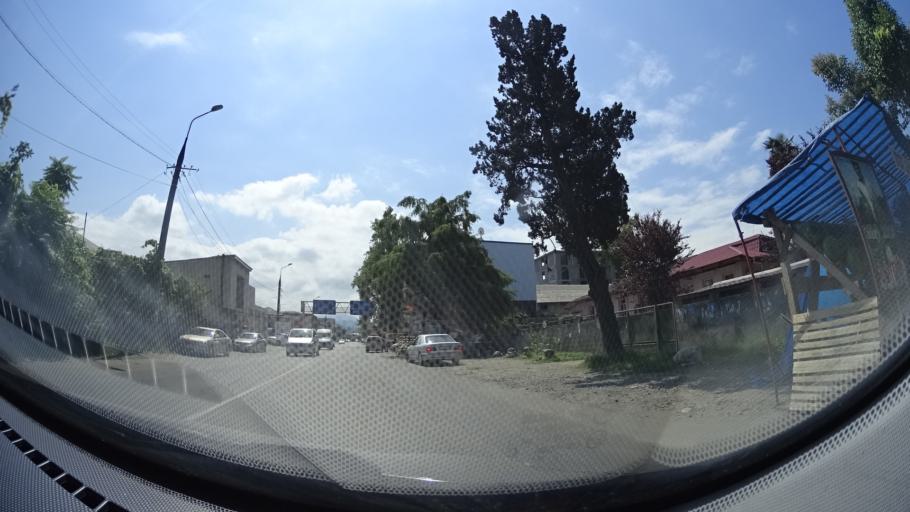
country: GE
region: Ajaria
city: Batumi
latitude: 41.6242
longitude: 41.6124
